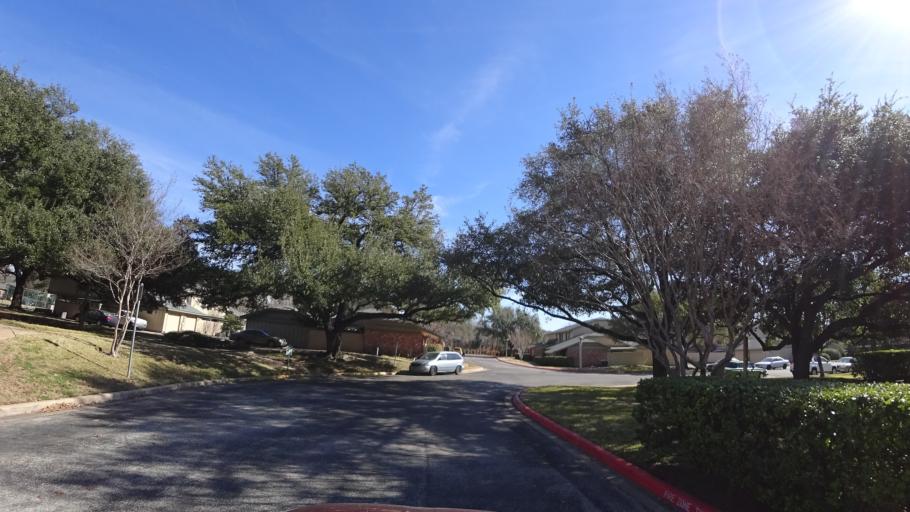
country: US
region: Texas
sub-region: Travis County
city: Wells Branch
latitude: 30.3689
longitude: -97.6983
